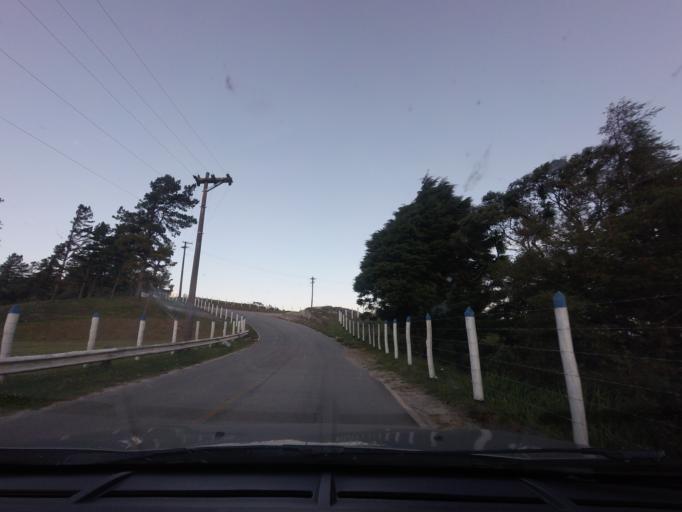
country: BR
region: Sao Paulo
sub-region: Campos Do Jordao
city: Campos do Jordao
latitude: -22.7710
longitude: -45.5297
